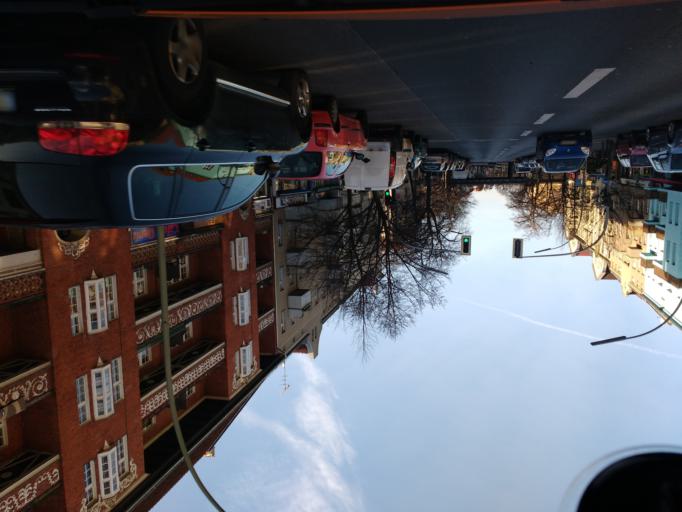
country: DE
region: Berlin
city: Pankow
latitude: 52.5636
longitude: 13.3916
